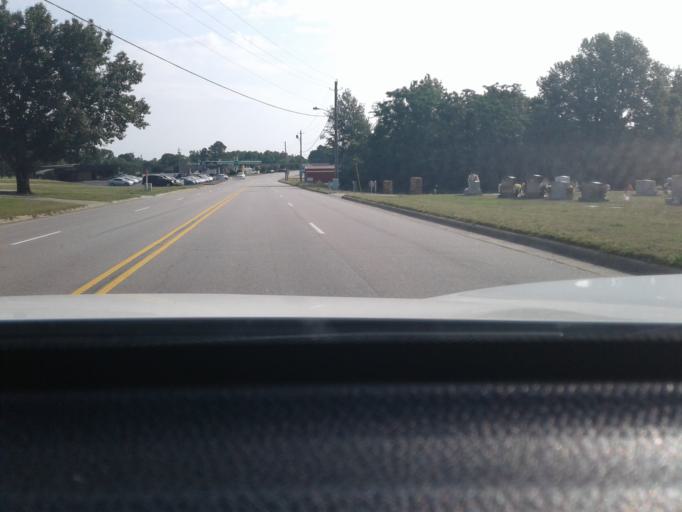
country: US
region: North Carolina
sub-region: Johnston County
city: Benson
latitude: 35.3871
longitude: -78.5446
